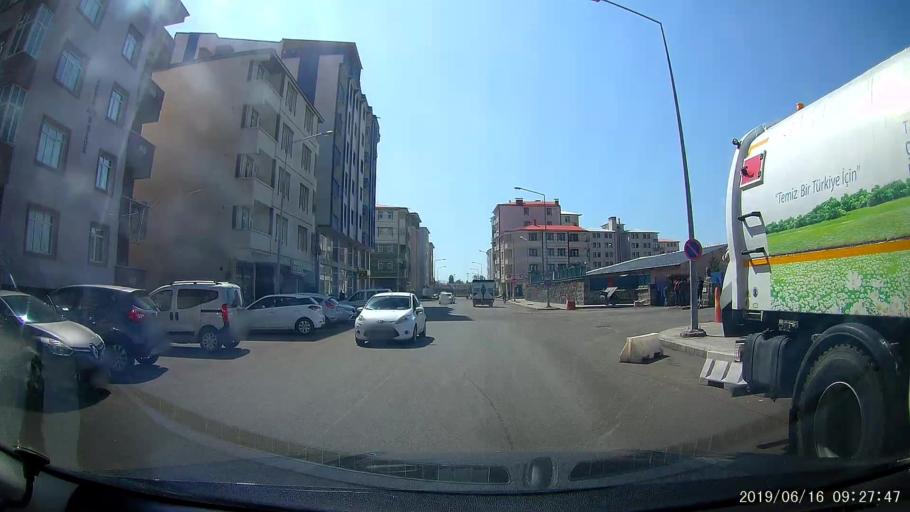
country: TR
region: Kars
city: Kars
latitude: 40.6049
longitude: 43.1025
